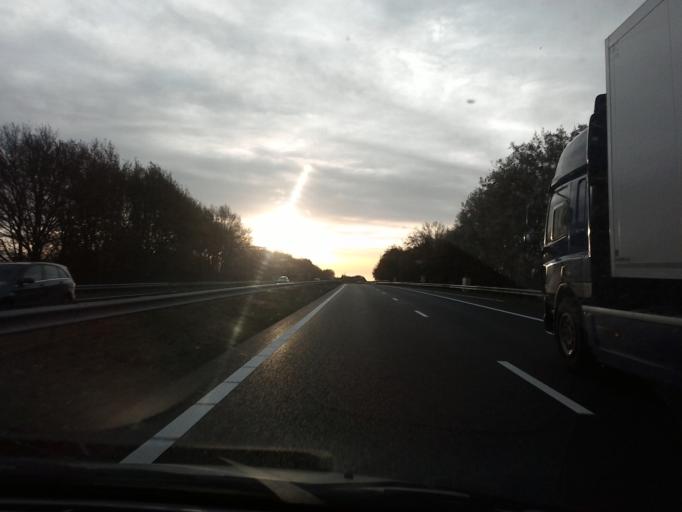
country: NL
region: North Brabant
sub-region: Gemeente Cranendonck
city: Cranendonck
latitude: 51.3133
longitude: 5.6048
